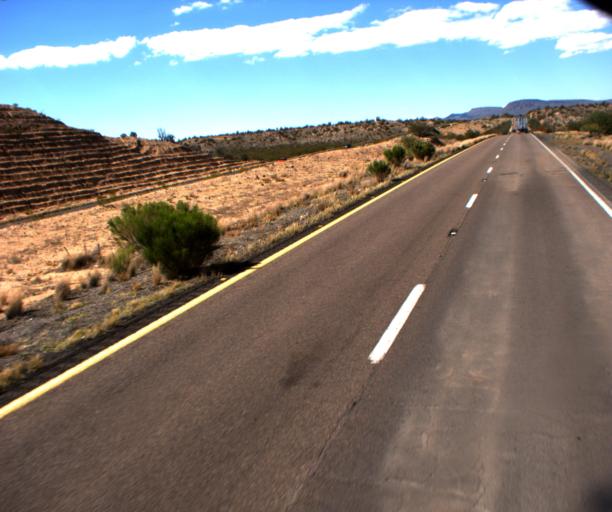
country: US
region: Arizona
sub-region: Mohave County
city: Kingman
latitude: 35.0820
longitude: -113.6654
